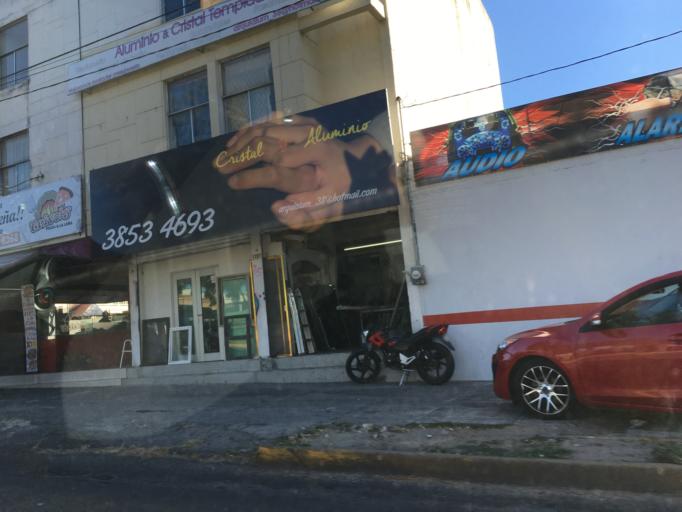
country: MX
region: Jalisco
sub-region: Zapopan
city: Zapopan
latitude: 20.7067
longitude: -103.3525
